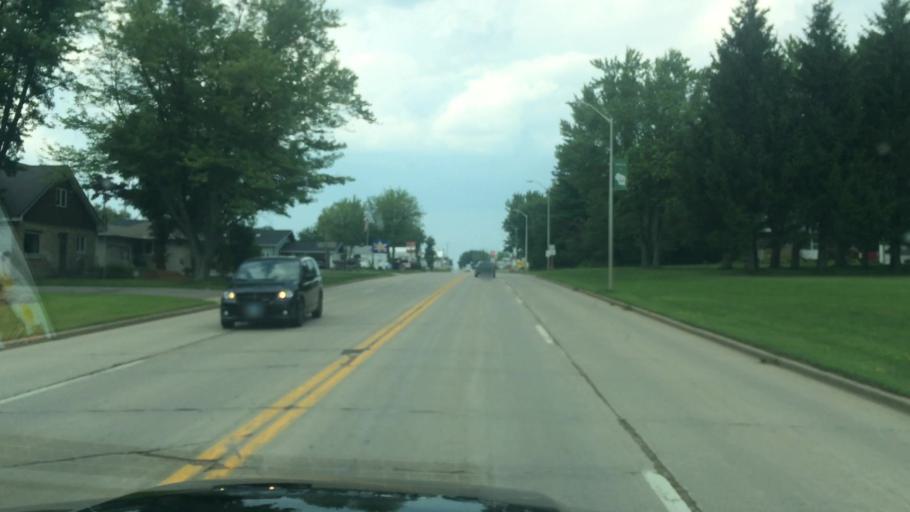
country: US
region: Wisconsin
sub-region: Clark County
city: Colby
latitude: 44.8989
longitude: -90.3150
